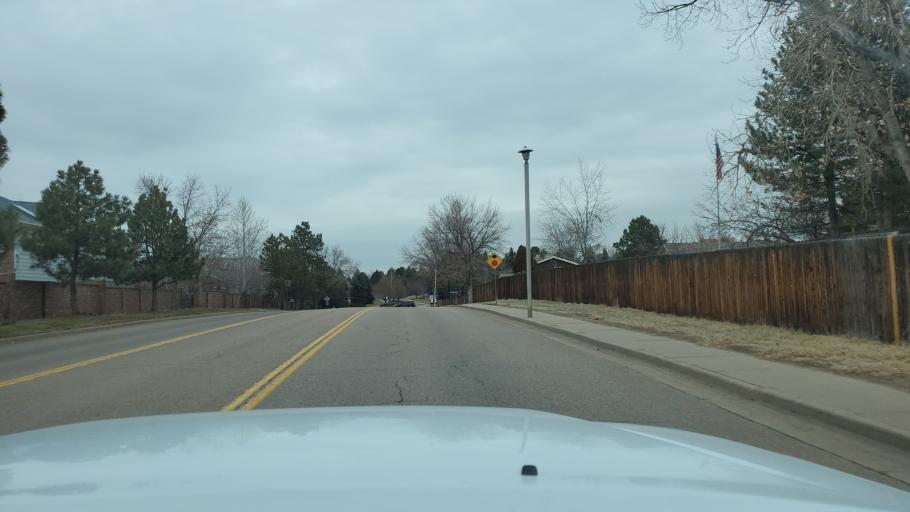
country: US
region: Colorado
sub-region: Arapahoe County
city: Greenwood Village
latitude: 39.6081
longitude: -104.9367
